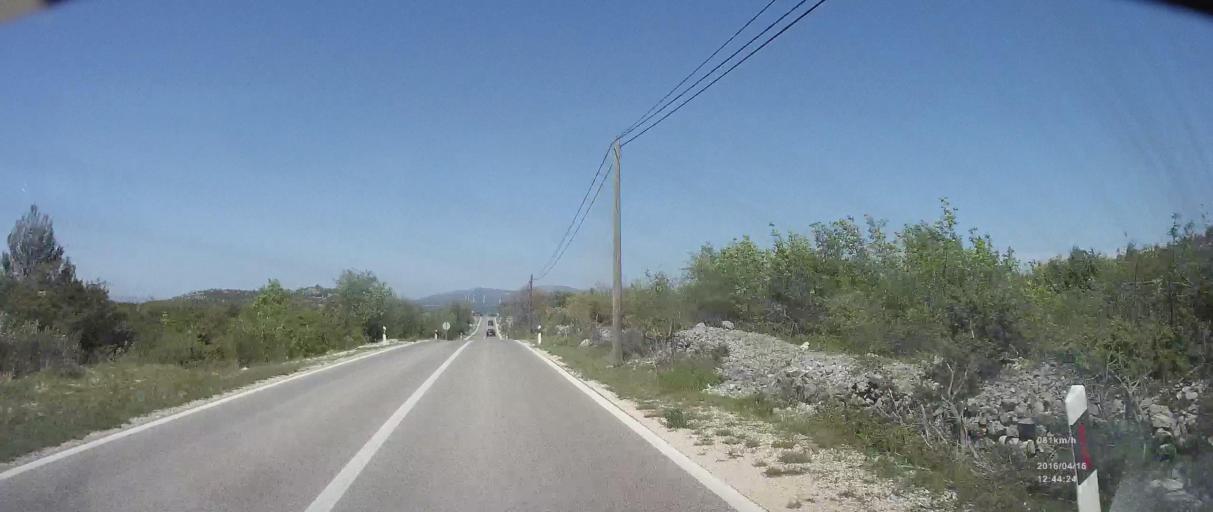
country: HR
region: Sibensko-Kniniska
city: Rogoznica
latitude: 43.6408
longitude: 16.0653
